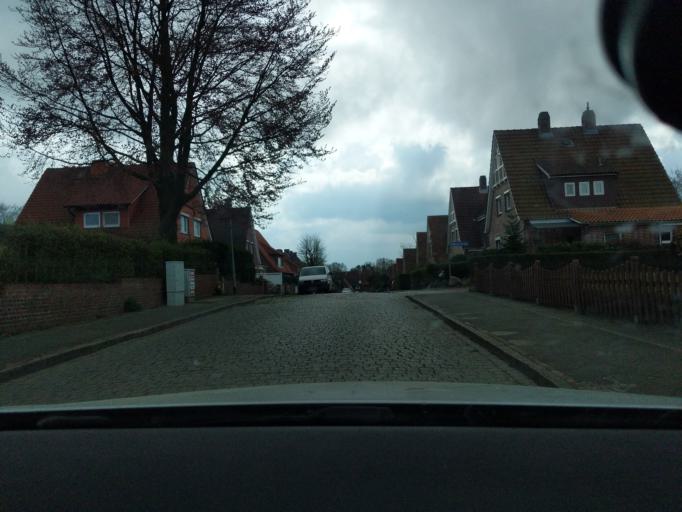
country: DE
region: Lower Saxony
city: Stade
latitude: 53.5874
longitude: 9.4702
